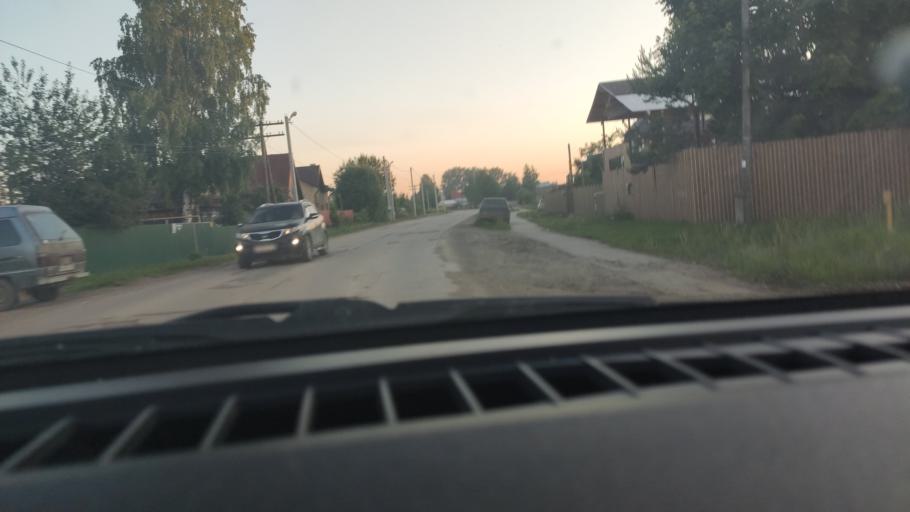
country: RU
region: Perm
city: Kultayevo
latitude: 57.8968
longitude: 55.9511
